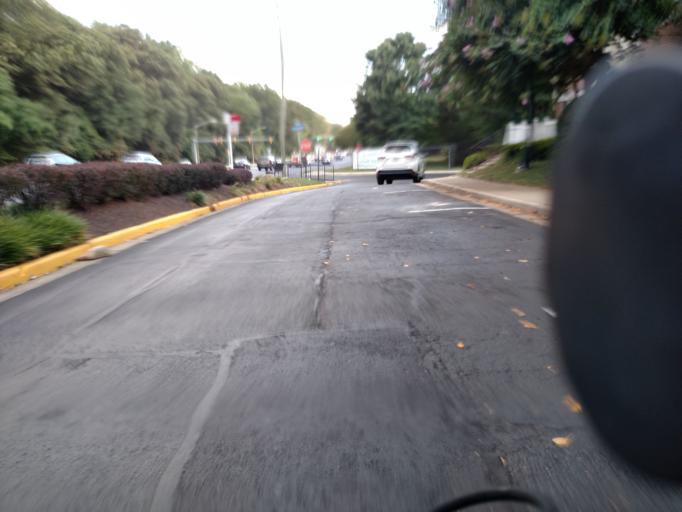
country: US
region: Virginia
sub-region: Fairfax County
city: Merrifield
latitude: 38.8600
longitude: -77.2266
